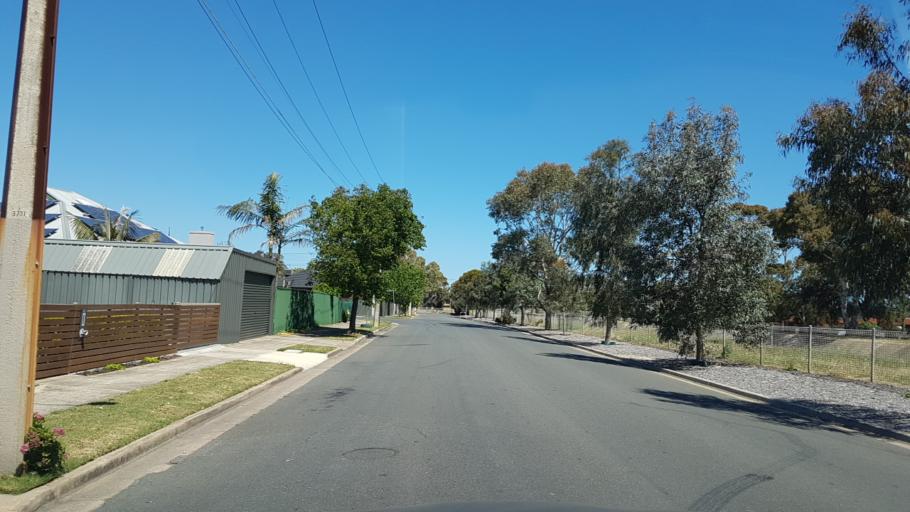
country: AU
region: South Australia
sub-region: Holdfast Bay
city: Glenelg East
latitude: -34.9692
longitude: 138.5246
